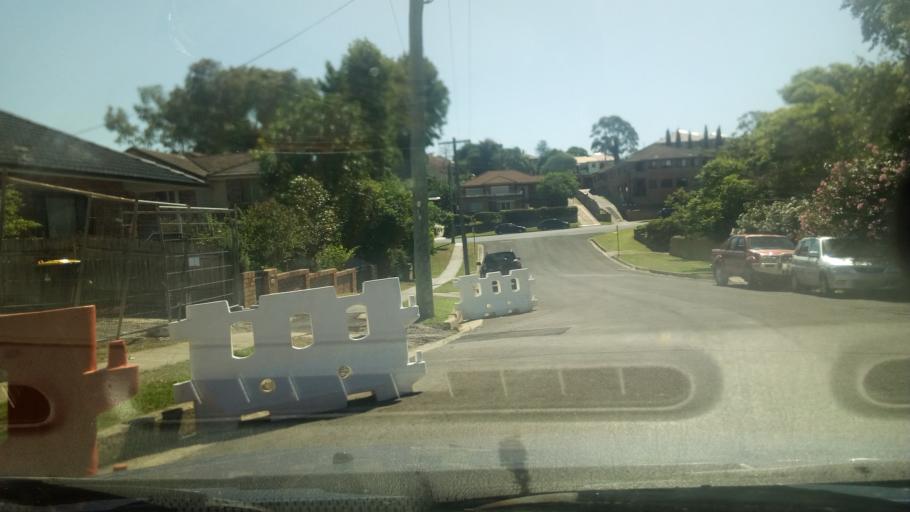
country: AU
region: New South Wales
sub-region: Wollongong
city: Gwynneville
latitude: -34.4231
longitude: 150.8813
